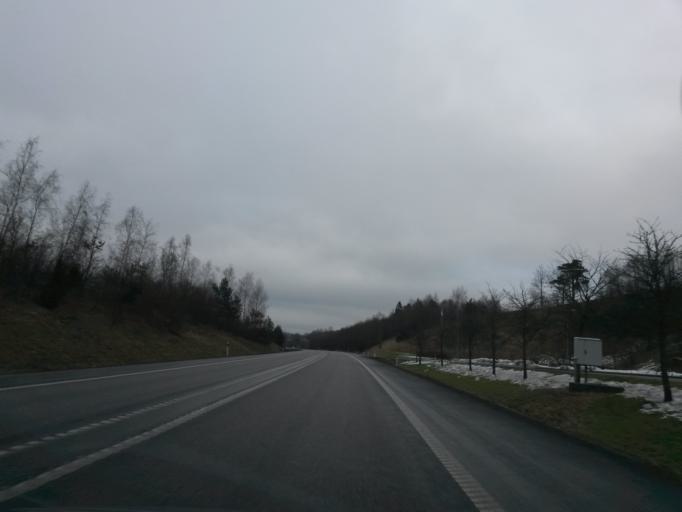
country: SE
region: Vaestra Goetaland
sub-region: Marks Kommun
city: Kinna
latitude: 57.4893
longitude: 12.6851
